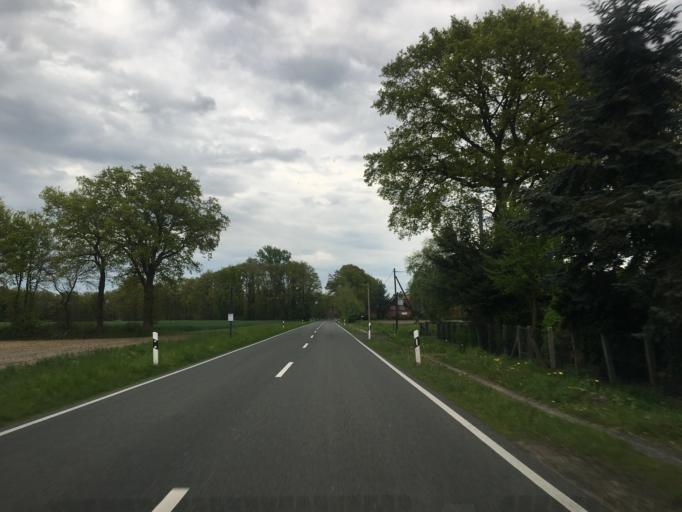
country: DE
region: North Rhine-Westphalia
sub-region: Regierungsbezirk Munster
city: Steinfurt
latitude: 52.1650
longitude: 7.3609
